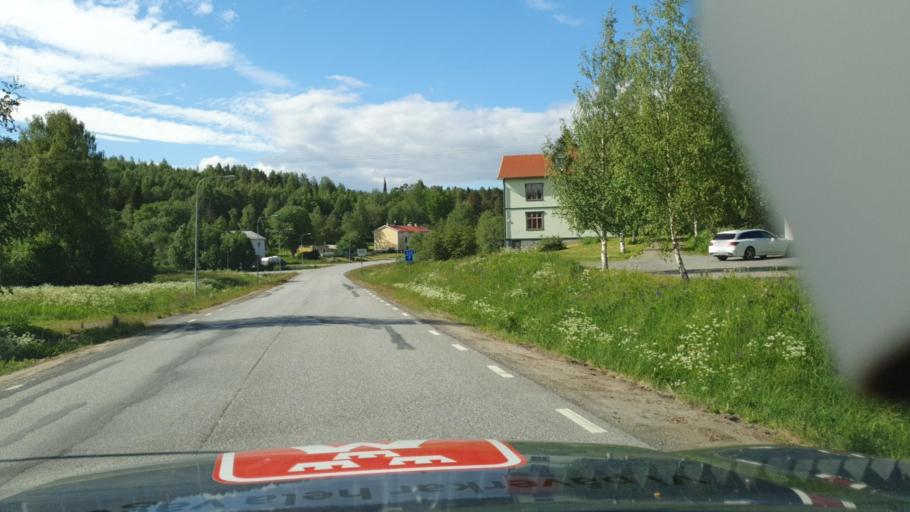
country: SE
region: Vaesternorrland
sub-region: Haernoesands Kommun
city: Haernoesand
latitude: 62.8125
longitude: 17.9534
